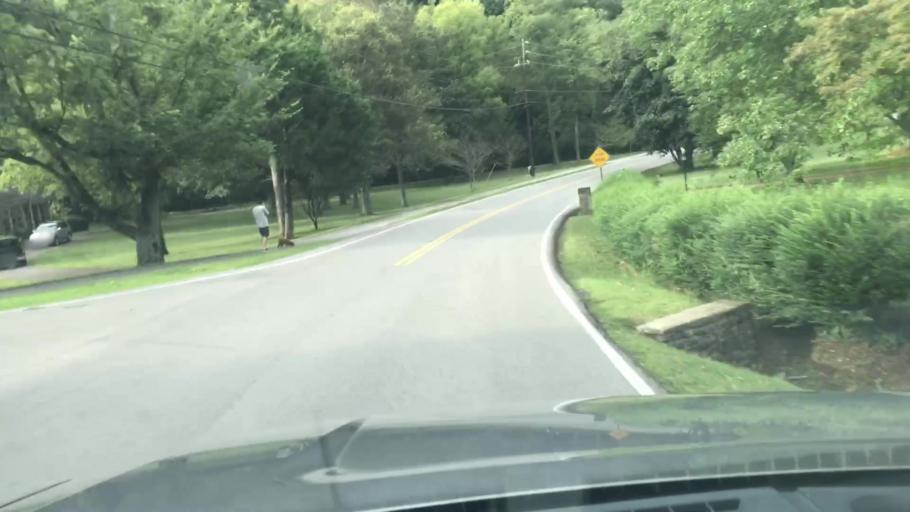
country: US
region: Tennessee
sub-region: Davidson County
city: Forest Hills
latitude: 36.0647
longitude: -86.8250
